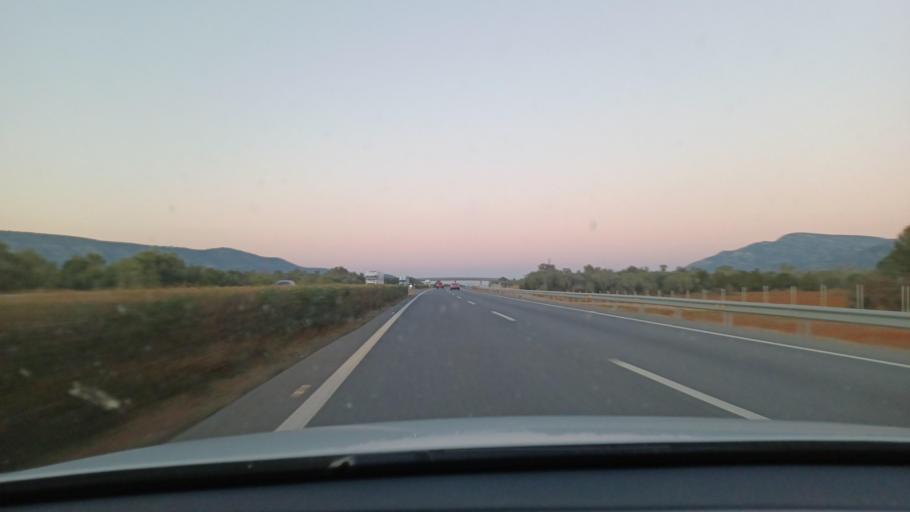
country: ES
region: Catalonia
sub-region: Provincia de Tarragona
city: Ulldecona
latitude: 40.6097
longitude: 0.4763
